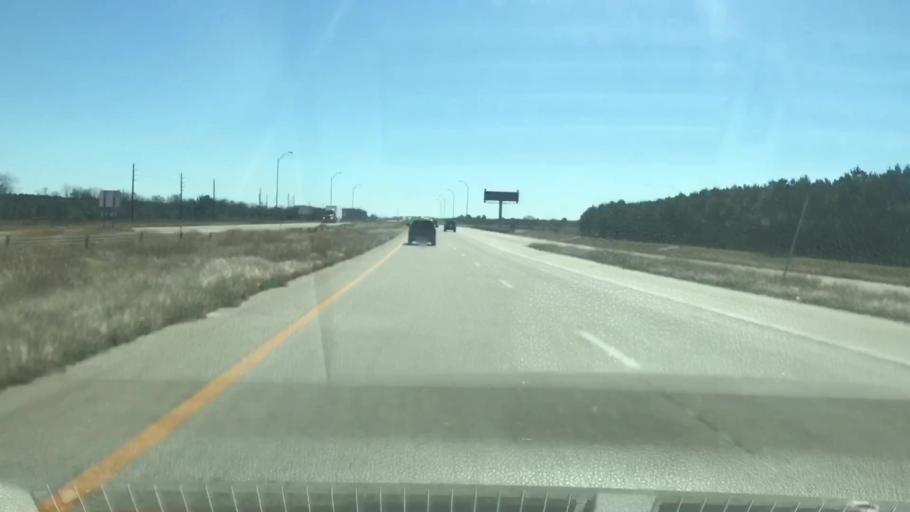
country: US
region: Texas
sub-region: Harris County
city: Cypress
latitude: 29.9013
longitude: -95.7584
